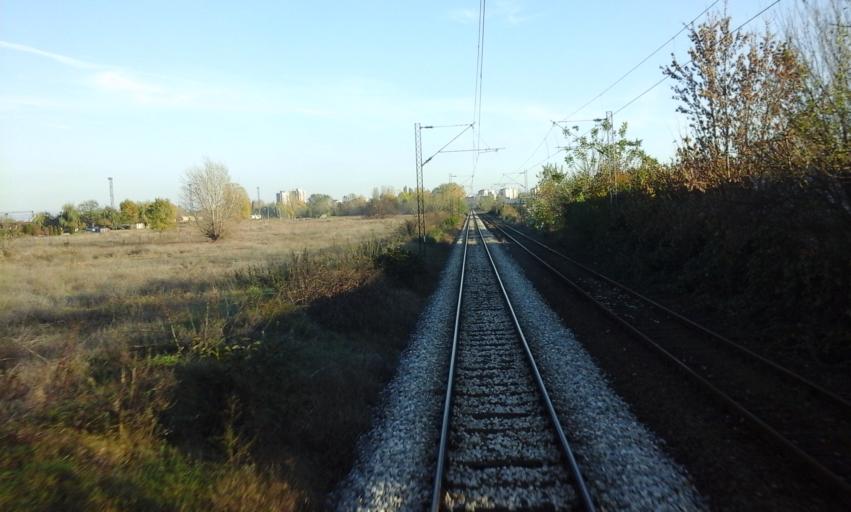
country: RS
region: Autonomna Pokrajina Vojvodina
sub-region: Juznobacki Okrug
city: Novi Sad
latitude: 45.2712
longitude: 19.8095
